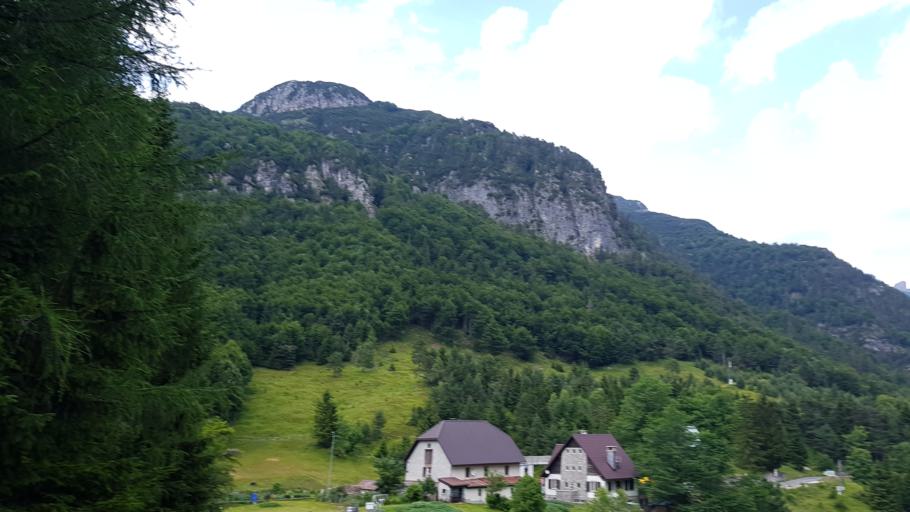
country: SI
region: Bovec
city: Bovec
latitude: 46.4176
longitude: 13.5782
